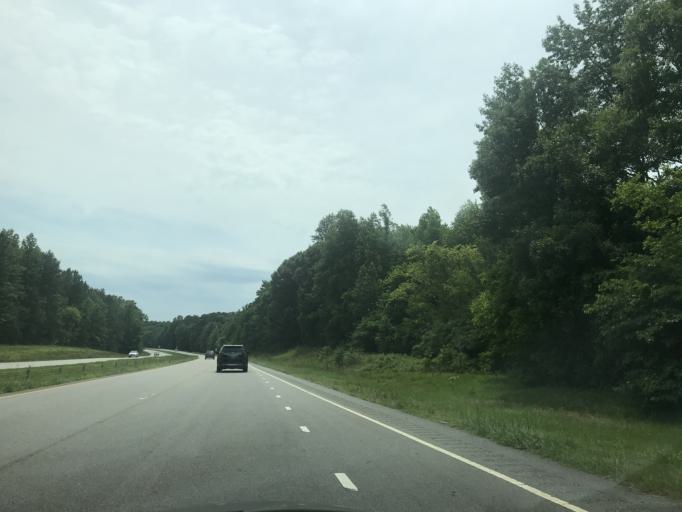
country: US
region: North Carolina
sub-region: Vance County
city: South Henderson
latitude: 36.2701
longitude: -78.4116
